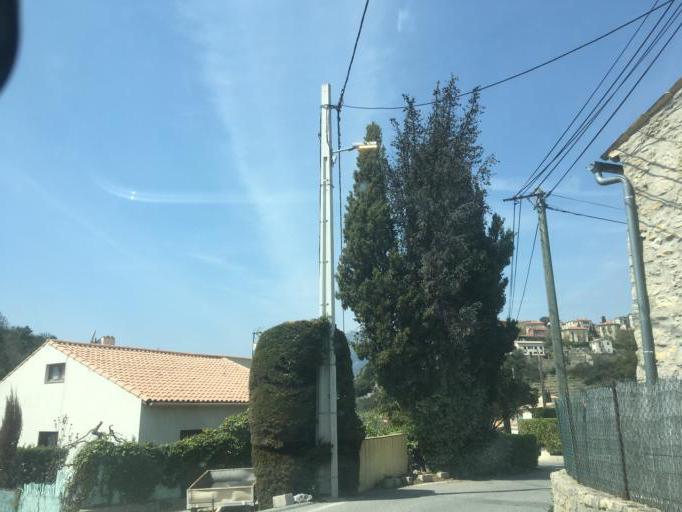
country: FR
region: Provence-Alpes-Cote d'Azur
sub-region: Departement des Alpes-Maritimes
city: Levens
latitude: 43.8547
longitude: 7.2297
